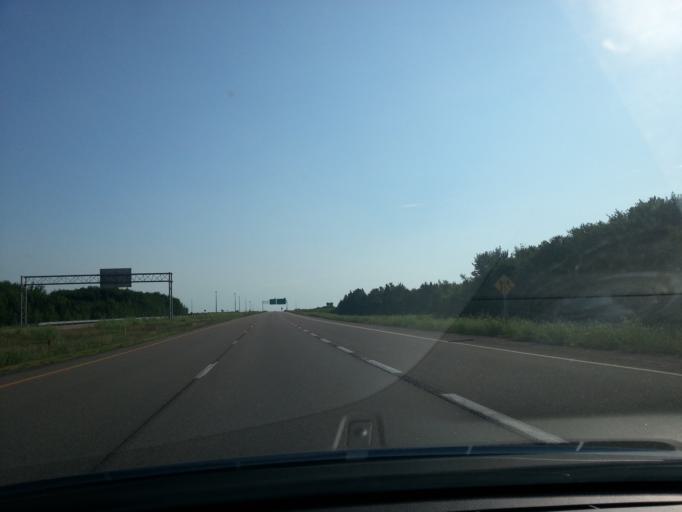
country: CA
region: New Brunswick
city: Dieppe
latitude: 46.1205
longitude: -64.6911
